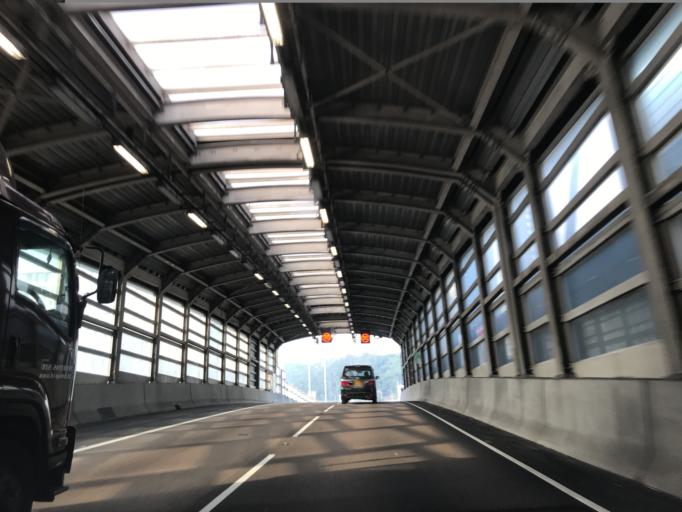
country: HK
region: Sham Shui Po
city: Sham Shui Po
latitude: 22.3342
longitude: 114.1445
